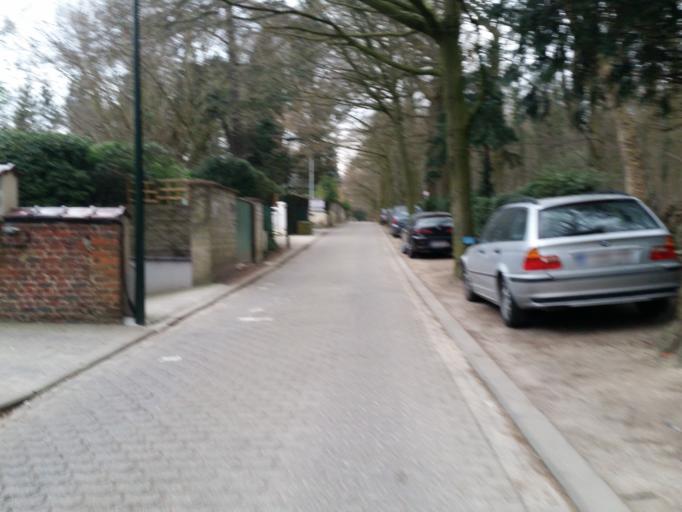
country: BE
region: Flanders
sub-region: Provincie Vlaams-Brabant
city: Linkebeek
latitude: 50.7999
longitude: 4.3787
